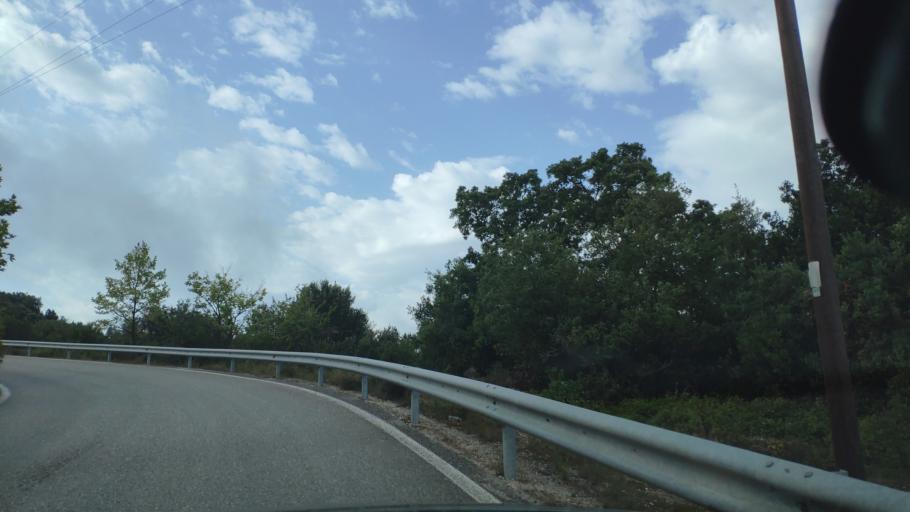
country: GR
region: West Greece
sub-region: Nomos Aitolias kai Akarnanias
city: Sardinia
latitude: 38.8775
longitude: 21.2649
